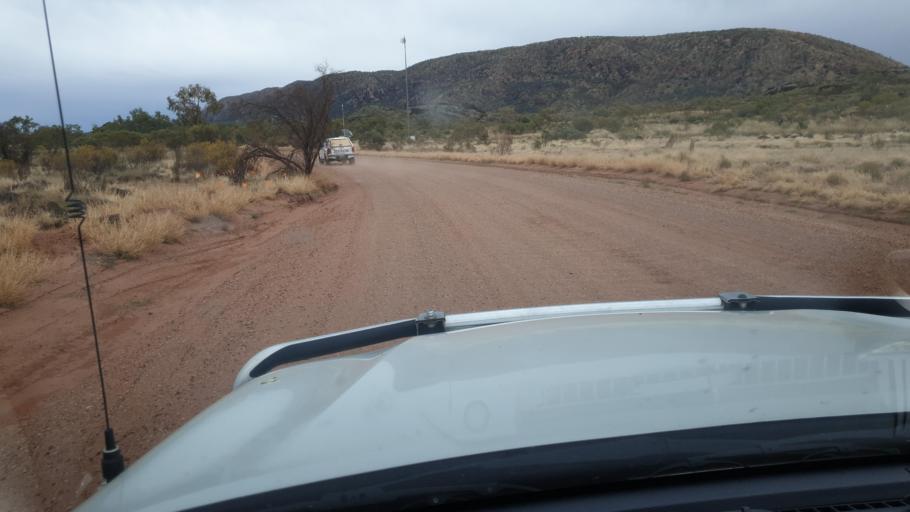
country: AU
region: Northern Territory
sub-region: Alice Springs
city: Alice Springs
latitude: -23.7893
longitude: 133.0770
